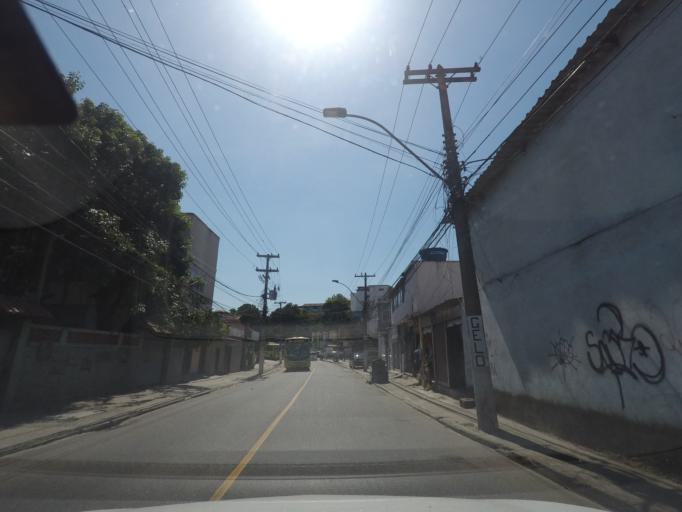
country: BR
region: Rio de Janeiro
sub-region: Niteroi
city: Niteroi
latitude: -22.9058
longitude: -43.0694
